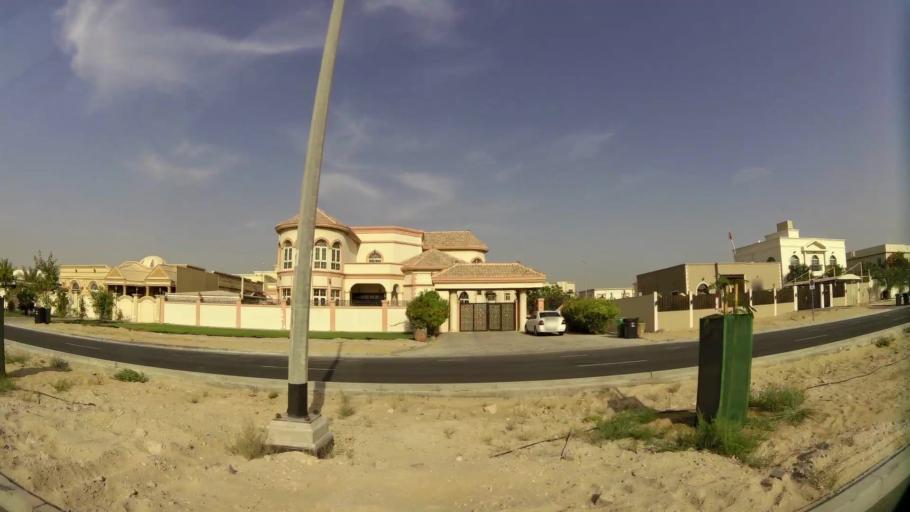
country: AE
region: Ash Shariqah
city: Sharjah
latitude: 25.2425
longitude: 55.4191
